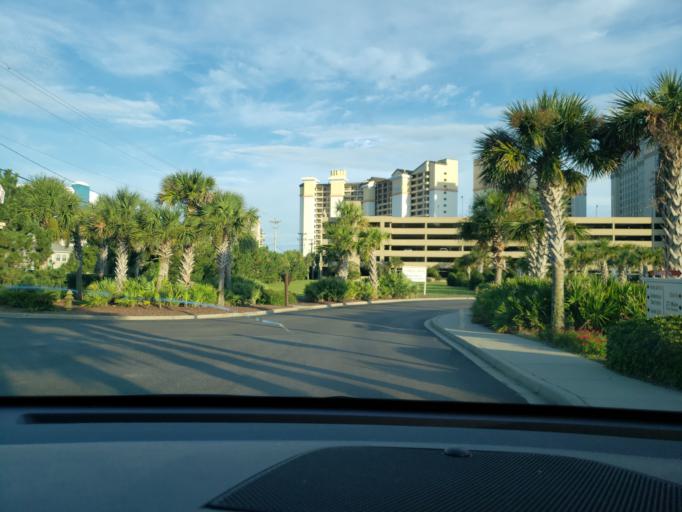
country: US
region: South Carolina
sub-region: Horry County
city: North Myrtle Beach
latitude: 33.7925
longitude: -78.7366
